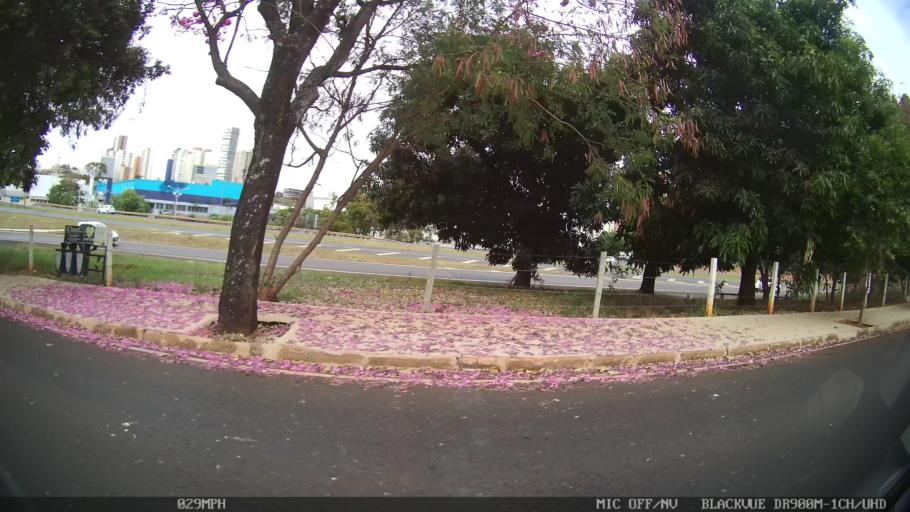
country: BR
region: Sao Paulo
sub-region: Sao Jose Do Rio Preto
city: Sao Jose do Rio Preto
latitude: -20.8231
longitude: -49.3869
